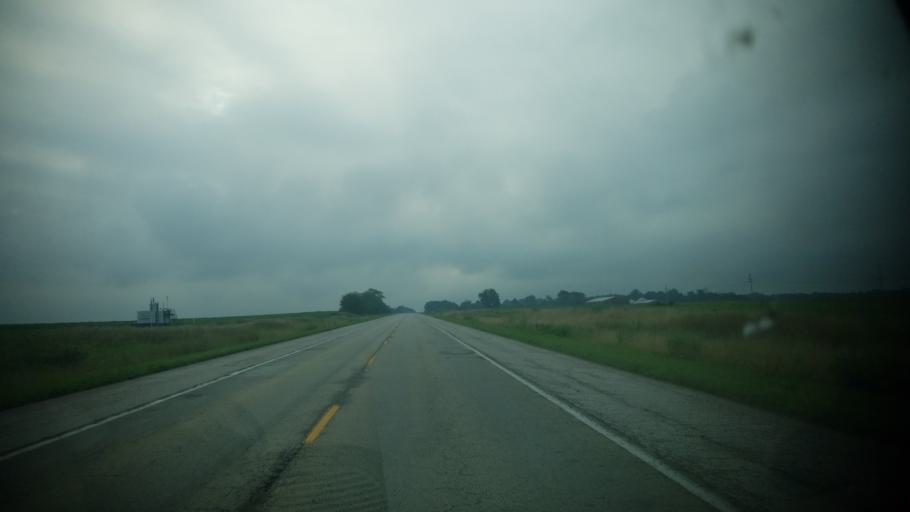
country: US
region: Illinois
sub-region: Clay County
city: Flora
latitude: 38.6772
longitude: -88.4120
